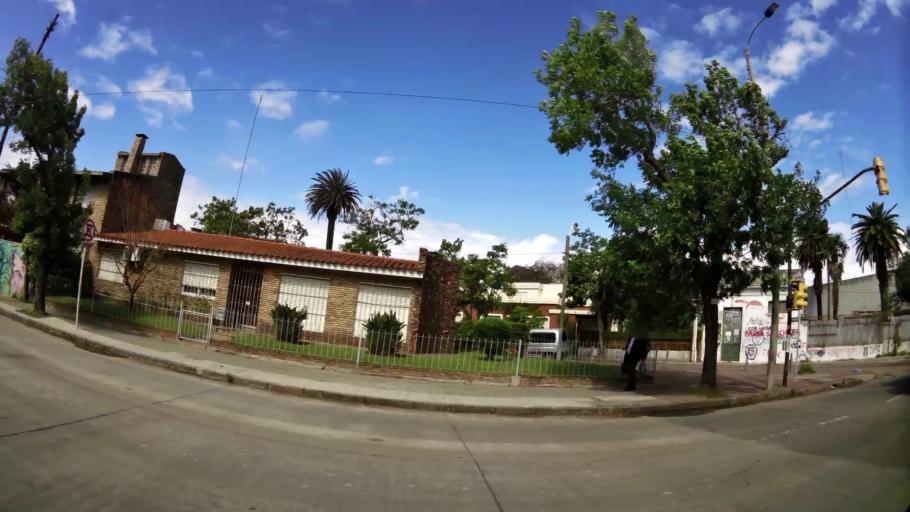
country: UY
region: Montevideo
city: Montevideo
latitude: -34.8641
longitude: -56.1929
